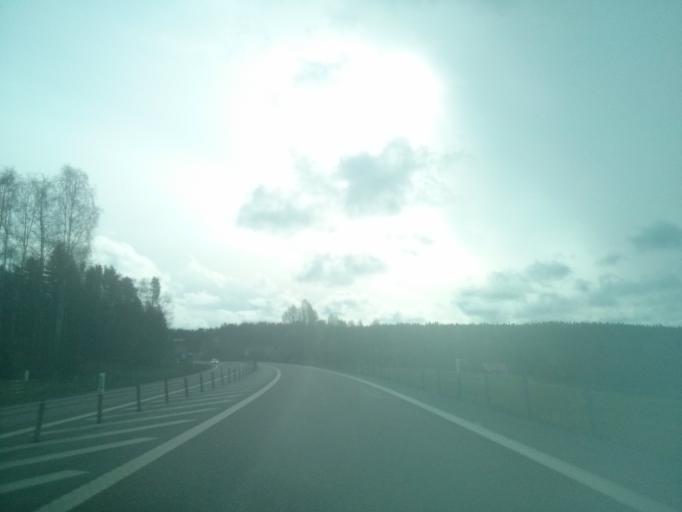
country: SE
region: Vaesternorrland
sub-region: Timra Kommun
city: Soraker
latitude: 62.5574
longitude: 17.6660
